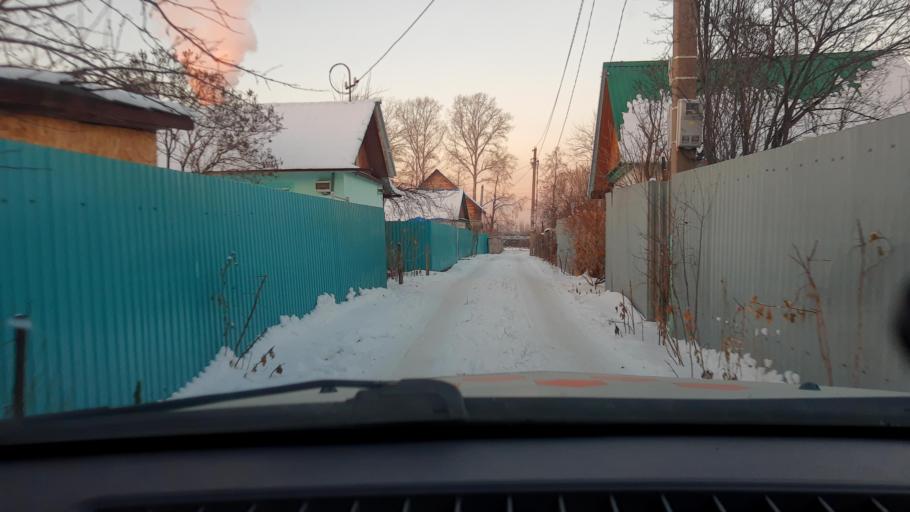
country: RU
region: Bashkortostan
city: Ufa
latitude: 54.8362
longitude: 56.1351
